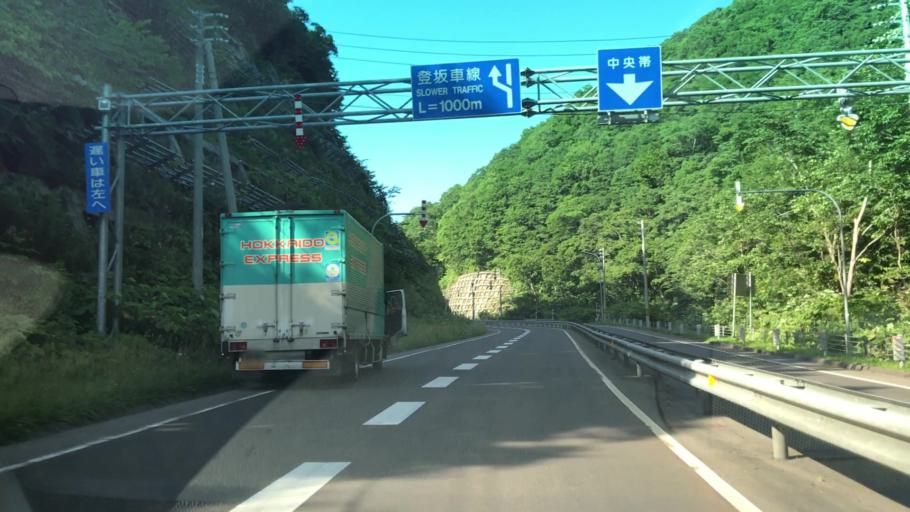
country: JP
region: Hokkaido
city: Iwanai
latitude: 43.0381
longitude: 140.6789
